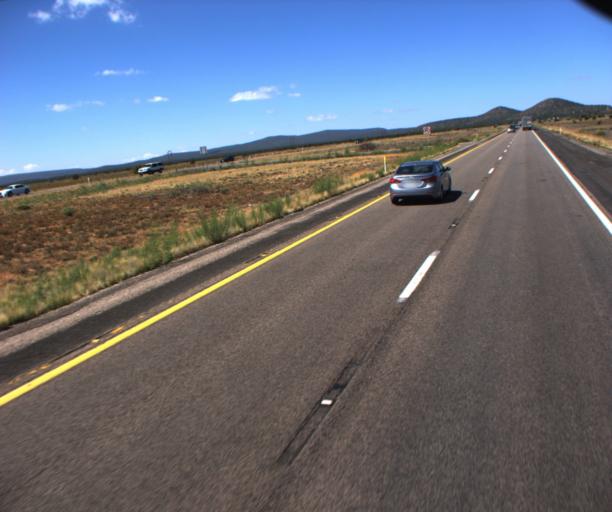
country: US
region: Arizona
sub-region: Mohave County
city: Peach Springs
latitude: 35.3094
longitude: -112.9829
